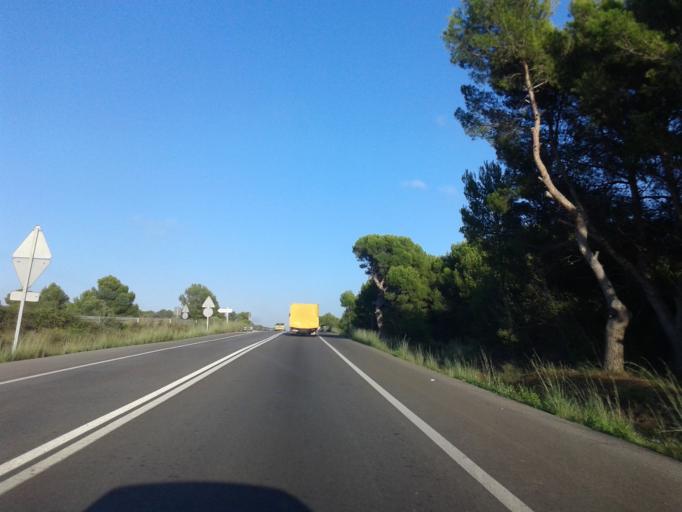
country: ES
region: Catalonia
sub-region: Provincia de Barcelona
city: Cubelles
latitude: 41.2097
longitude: 1.6824
